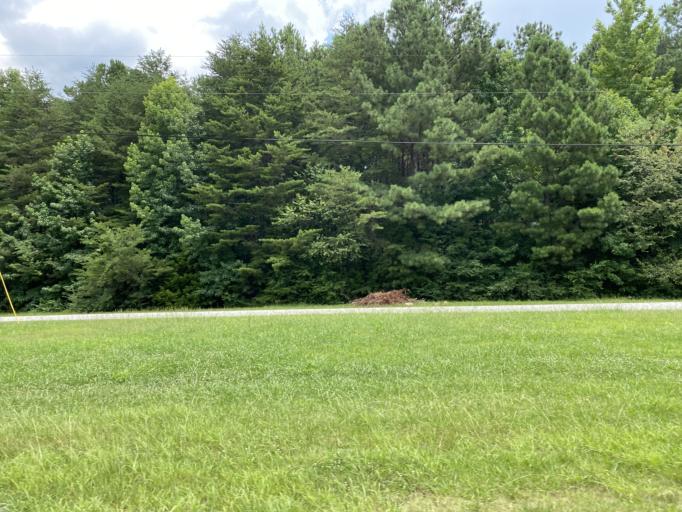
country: US
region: Alabama
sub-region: Madison County
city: Owens Cross Roads
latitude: 34.6531
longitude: -86.4799
